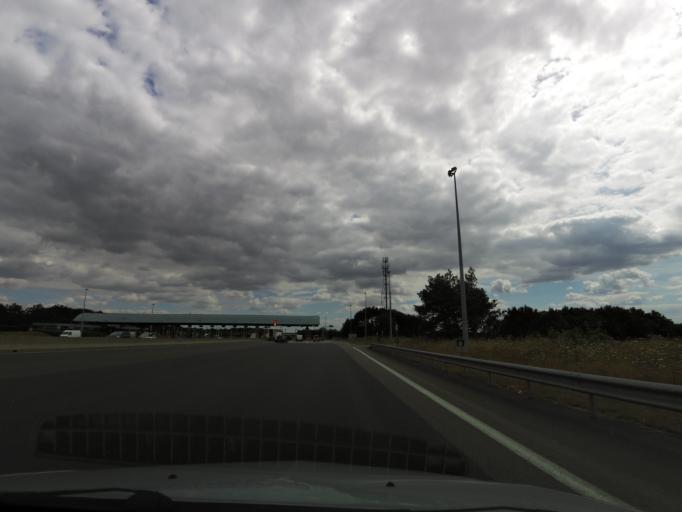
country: FR
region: Pays de la Loire
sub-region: Departement de la Loire-Atlantique
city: Le Bignon
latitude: 47.1157
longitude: -1.4933
